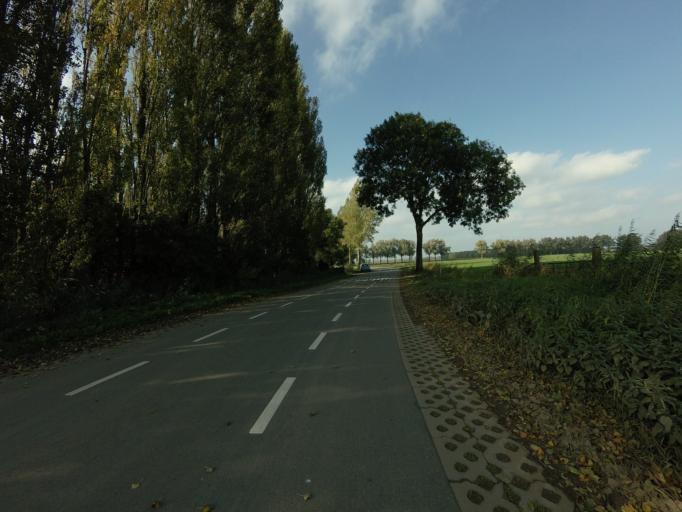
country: NL
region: Gelderland
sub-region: Gemeente Geldermalsen
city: Geldermalsen
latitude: 51.9148
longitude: 5.3062
